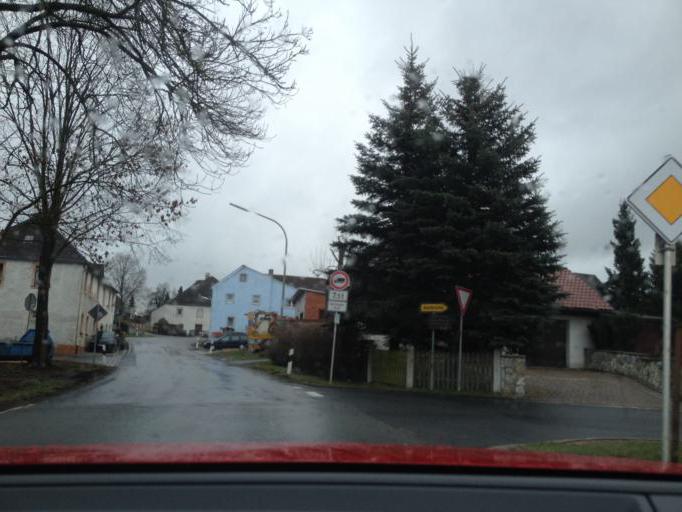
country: DE
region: Bavaria
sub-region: Upper Franconia
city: Thiersheim
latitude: 50.0810
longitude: 12.1575
